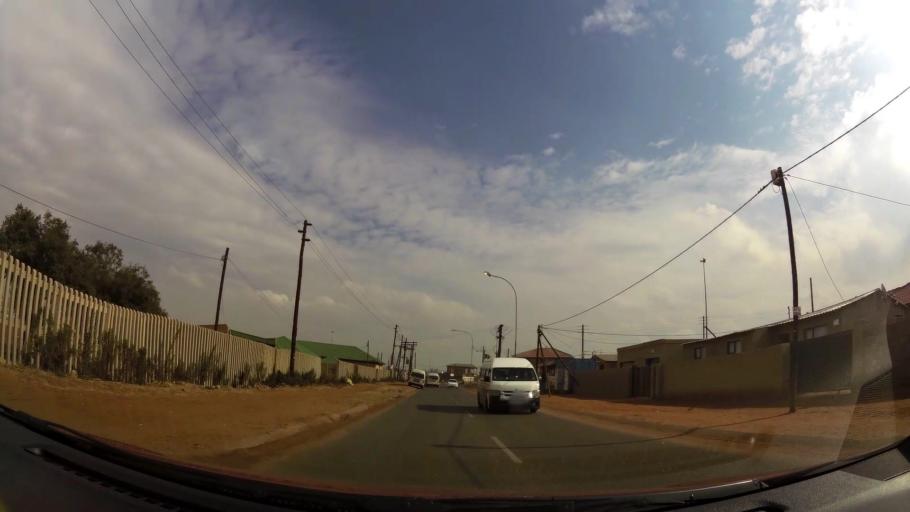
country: ZA
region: Gauteng
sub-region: City of Johannesburg Metropolitan Municipality
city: Soweto
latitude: -26.2599
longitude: 27.8210
